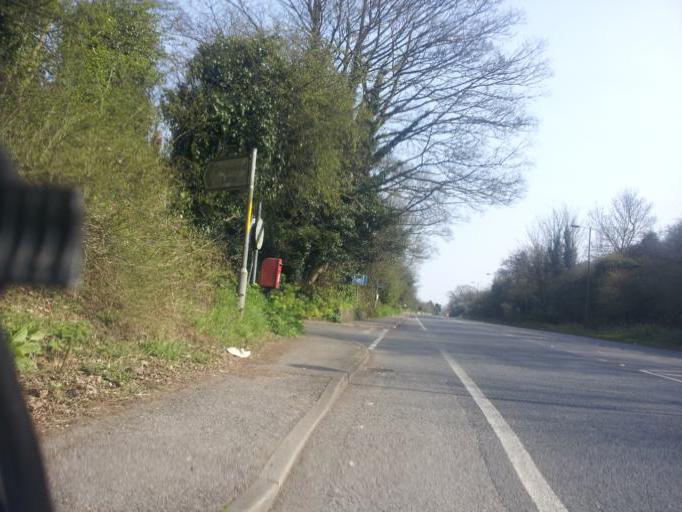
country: GB
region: England
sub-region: Kent
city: Strood
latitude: 51.4069
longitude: 0.4741
